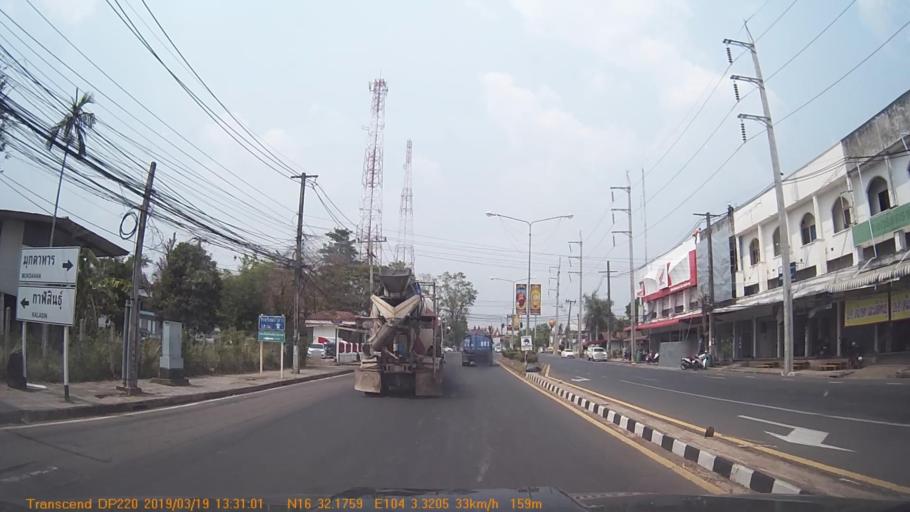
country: TH
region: Kalasin
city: Kuchinarai
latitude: 16.5364
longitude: 104.0553
